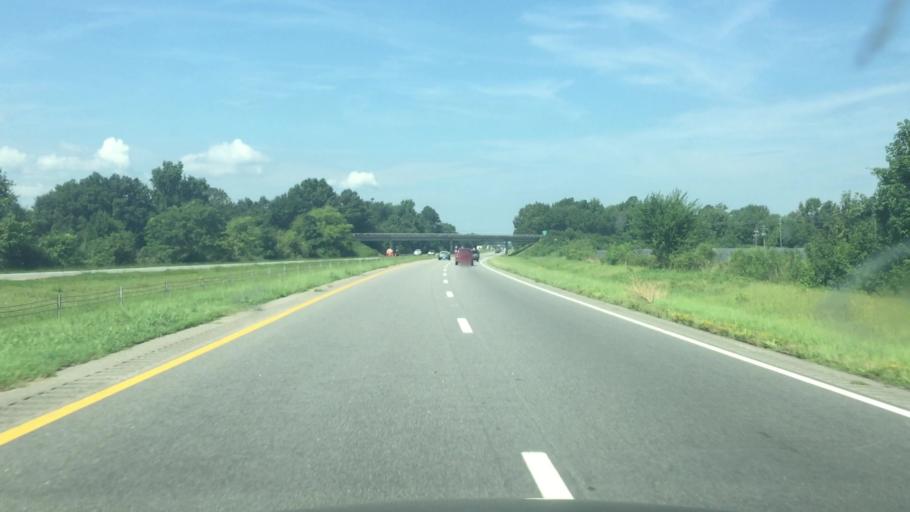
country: US
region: North Carolina
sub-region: Scotland County
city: Laurinburg
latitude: 34.7554
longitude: -79.4427
